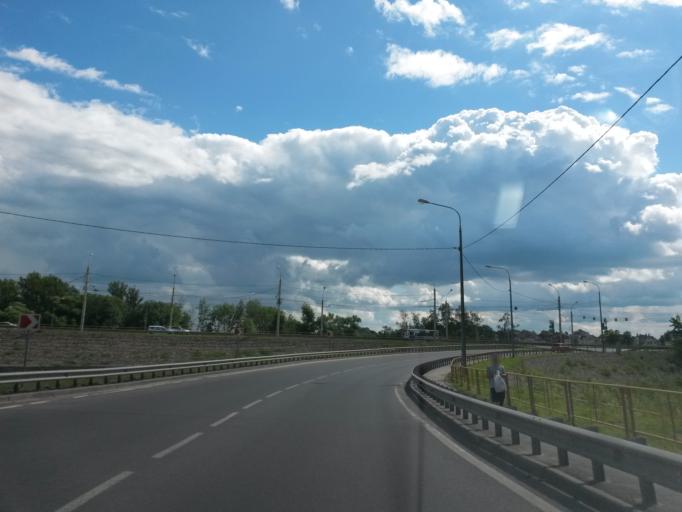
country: RU
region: Jaroslavl
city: Yaroslavl
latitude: 57.6187
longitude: 39.8839
